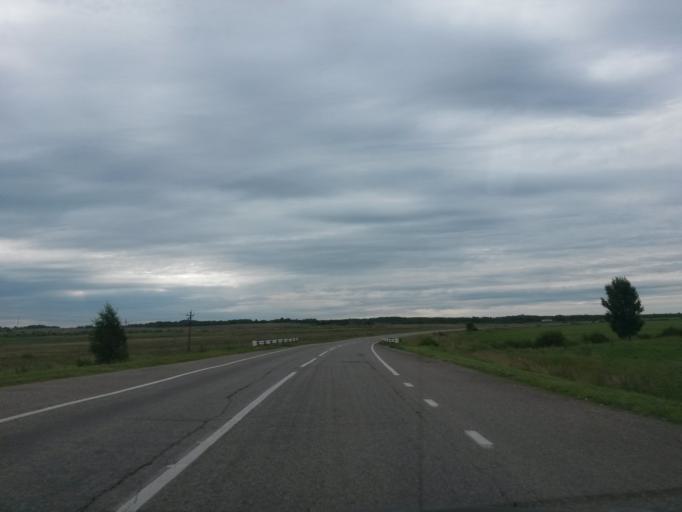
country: RU
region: Jaroslavl
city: Gavrilov-Yam
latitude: 57.3153
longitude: 39.8801
